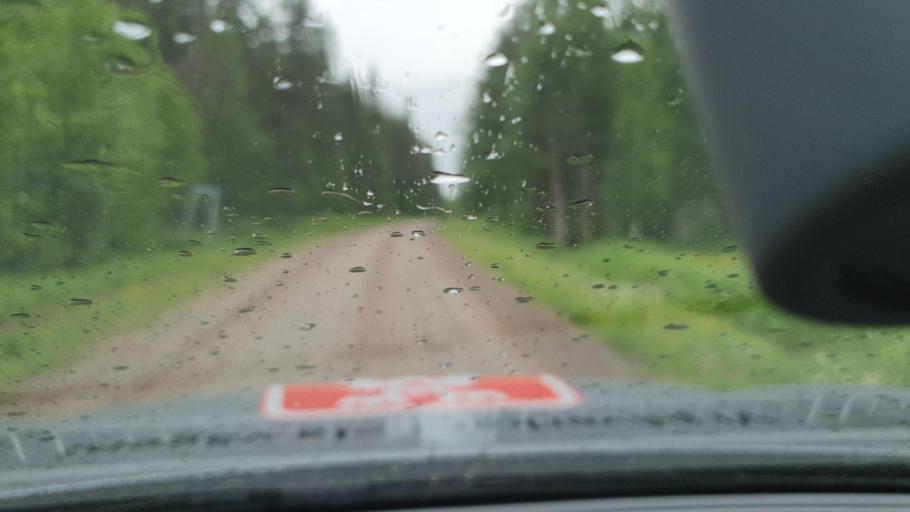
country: SE
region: Norrbotten
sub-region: Overkalix Kommun
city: OEverkalix
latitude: 66.5185
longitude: 22.7446
